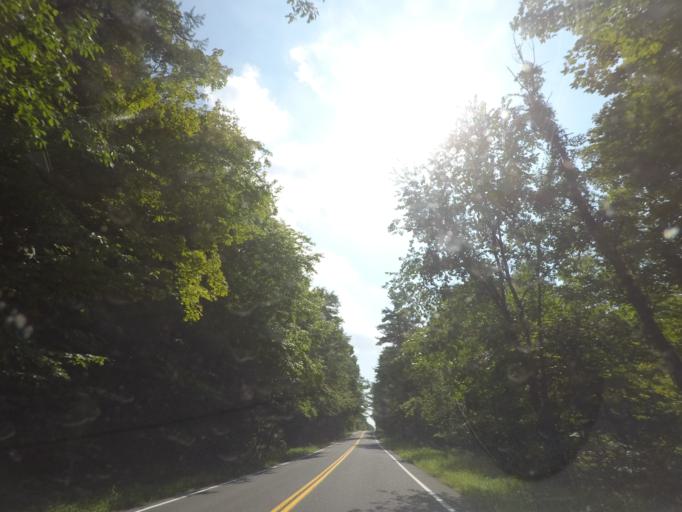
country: US
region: New York
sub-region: Rensselaer County
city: Poestenkill
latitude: 42.7987
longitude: -73.5280
